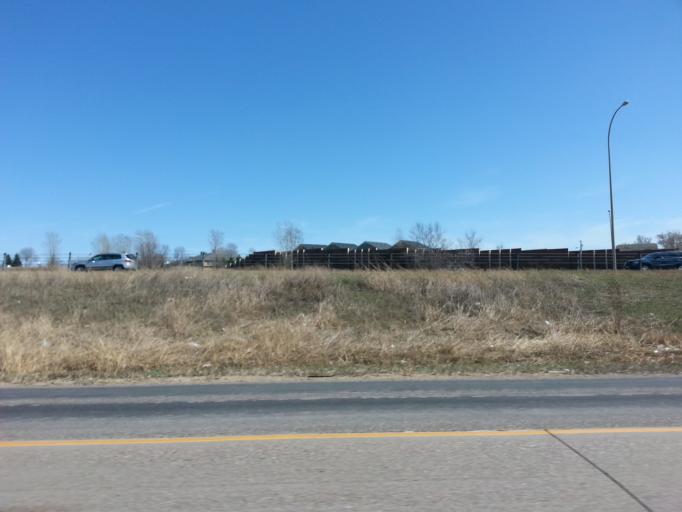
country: US
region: Minnesota
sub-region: Washington County
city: Woodbury
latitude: 44.9140
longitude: -92.9818
